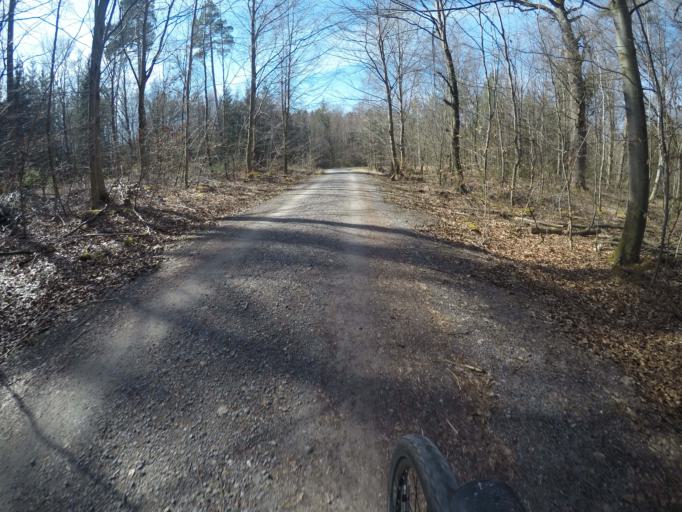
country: DE
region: Baden-Wuerttemberg
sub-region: Regierungsbezirk Stuttgart
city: Gerlingen
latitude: 48.7653
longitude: 9.0779
